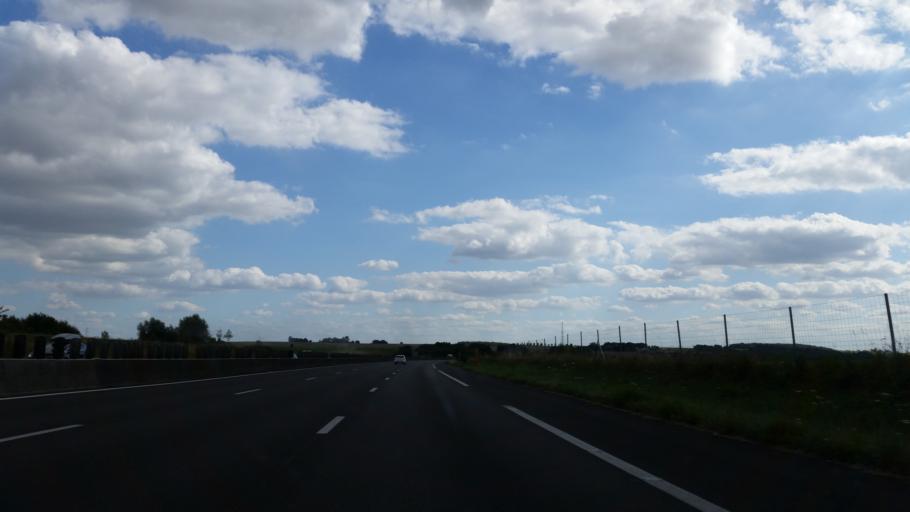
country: FR
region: Nord-Pas-de-Calais
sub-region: Departement du Pas-de-Calais
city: Bapaume
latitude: 50.0273
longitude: 2.8845
